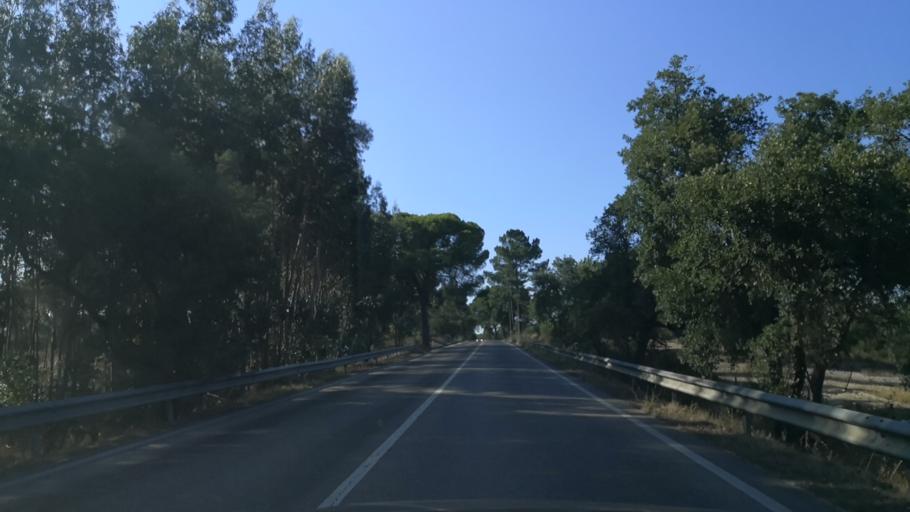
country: PT
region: Santarem
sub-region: Coruche
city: Coruche
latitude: 38.9740
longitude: -8.5391
